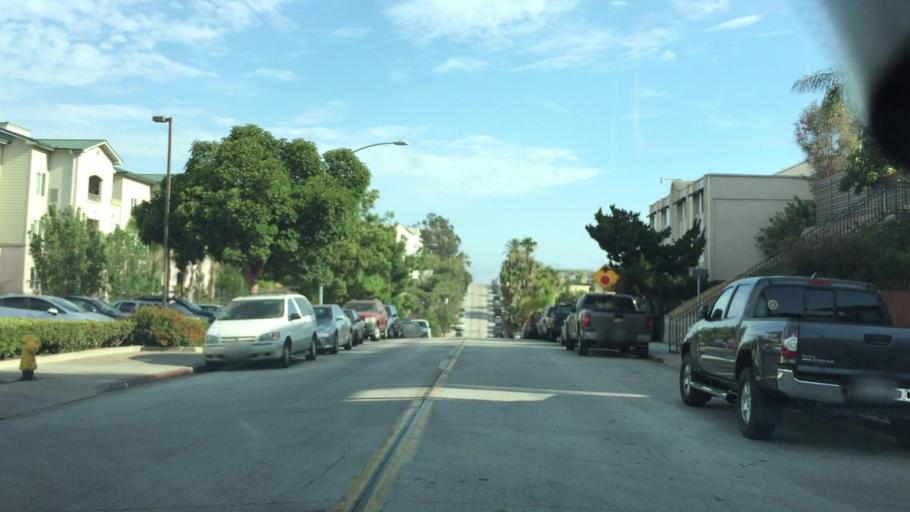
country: US
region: California
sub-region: San Diego County
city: Lemon Grove
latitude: 32.7561
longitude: -117.0837
